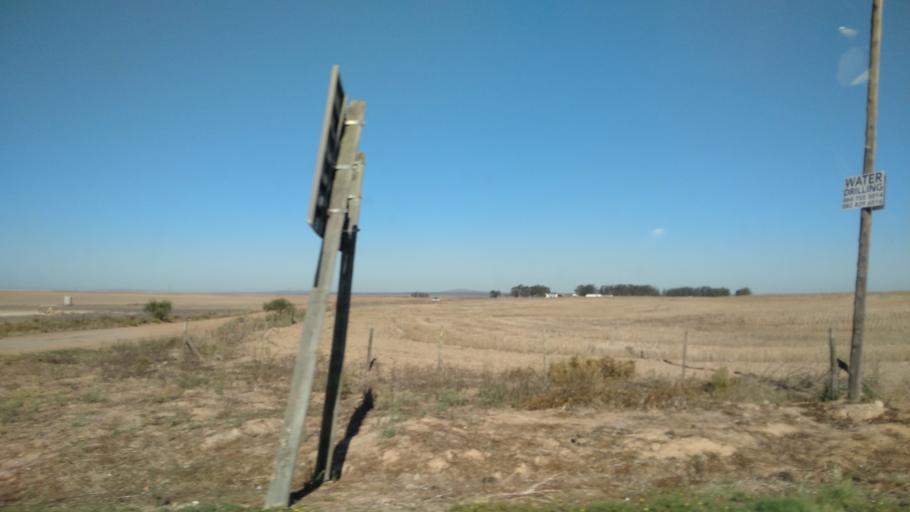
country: ZA
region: Western Cape
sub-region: West Coast District Municipality
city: Moorreesburg
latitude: -33.1357
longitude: 18.4545
